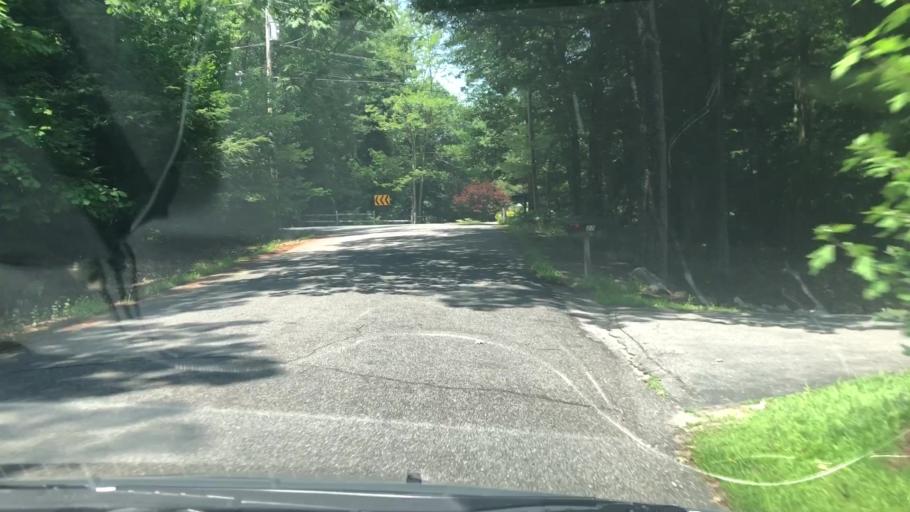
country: US
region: New Hampshire
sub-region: Hillsborough County
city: Milford
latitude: 42.8767
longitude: -71.6331
